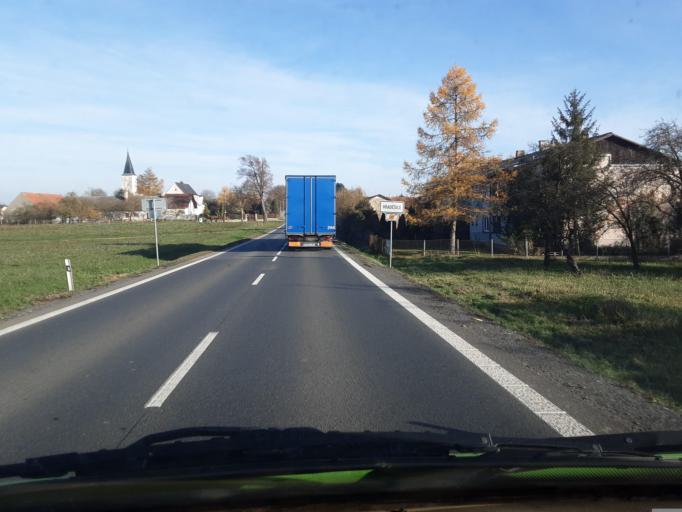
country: CZ
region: Plzensky
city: Horazd'ovice
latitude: 49.3248
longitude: 13.5932
